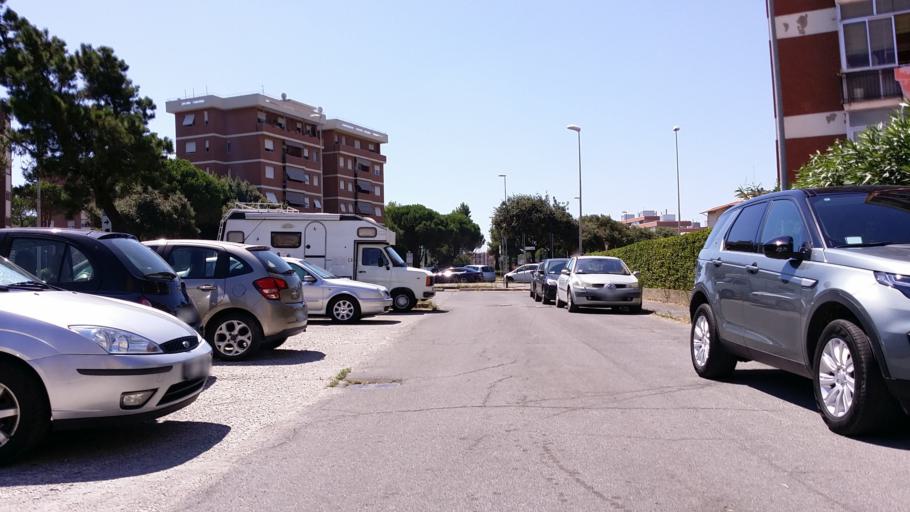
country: IT
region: Tuscany
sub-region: Provincia di Livorno
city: Livorno
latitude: 43.5437
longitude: 10.3307
